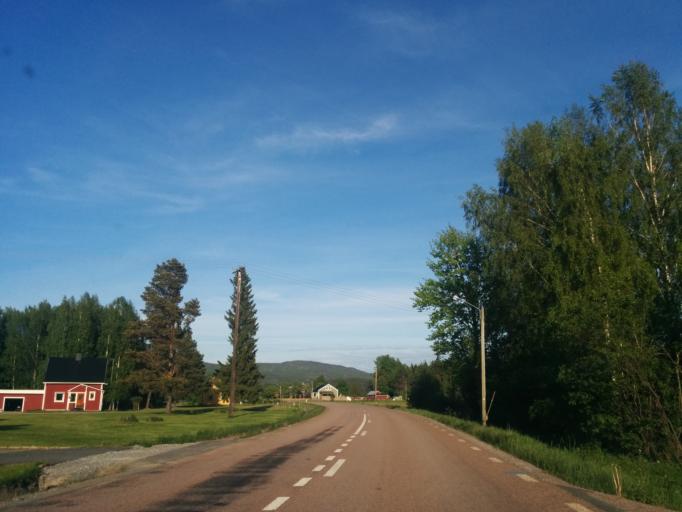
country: SE
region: Vaesternorrland
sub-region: Kramfors Kommun
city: Kramfors
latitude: 63.0227
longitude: 17.7910
